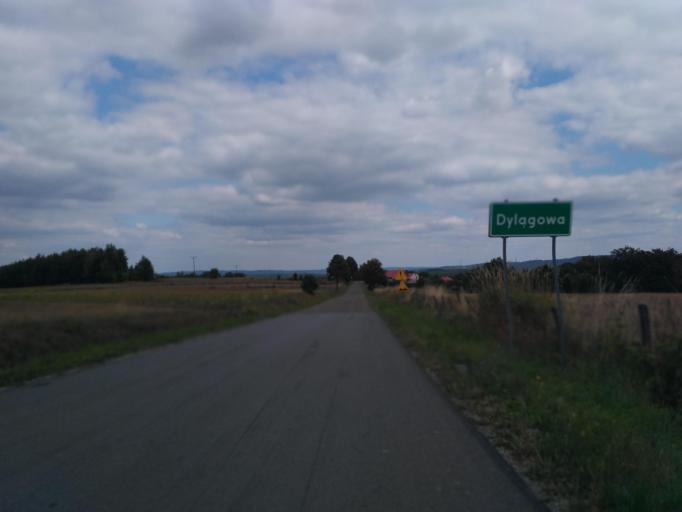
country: PL
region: Subcarpathian Voivodeship
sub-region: Powiat rzeszowski
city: Dynow
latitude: 49.7856
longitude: 22.2844
